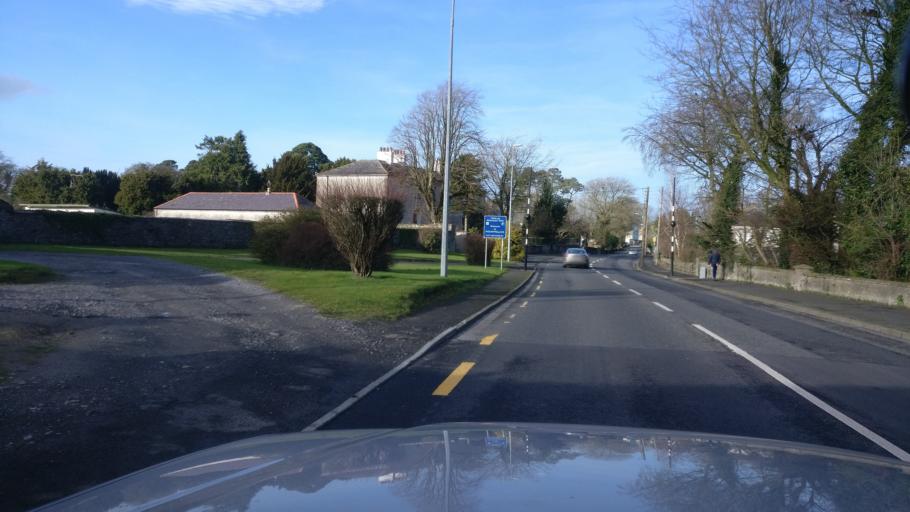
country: IE
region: Leinster
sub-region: Laois
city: Mountmellick
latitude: 53.1118
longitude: -7.3285
